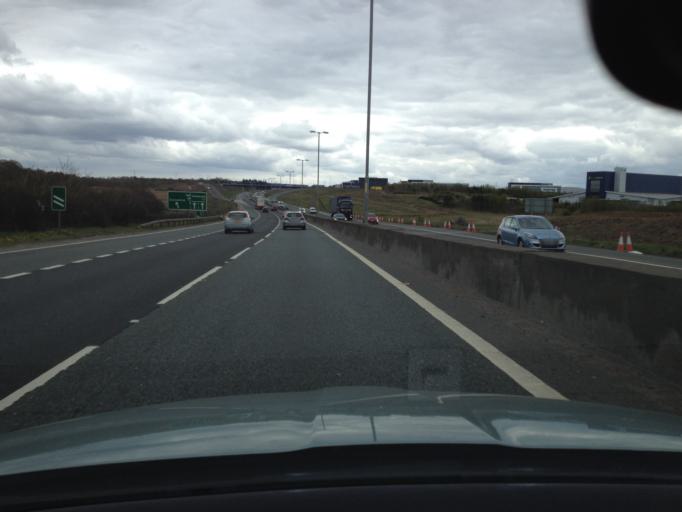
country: GB
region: Scotland
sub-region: North Lanarkshire
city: Bellshill
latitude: 55.8382
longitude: -3.9987
